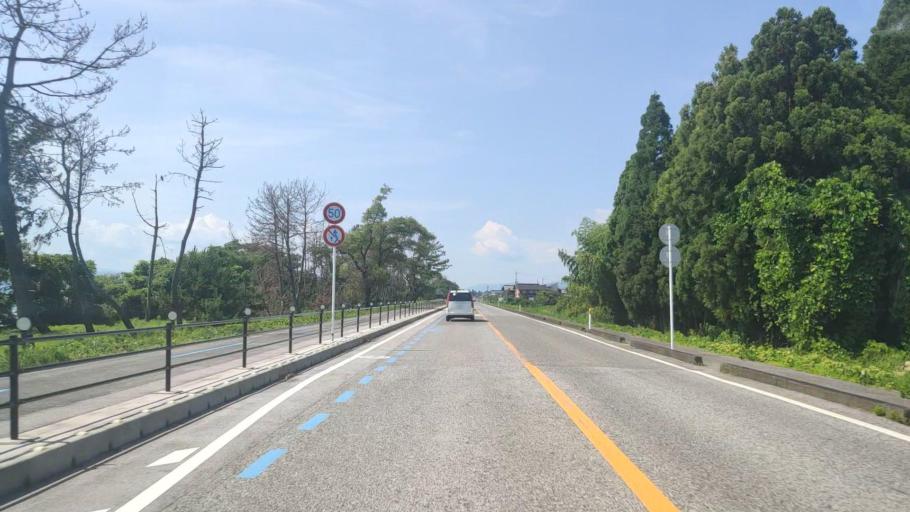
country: JP
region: Shiga Prefecture
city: Nagahama
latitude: 35.3987
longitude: 136.2173
